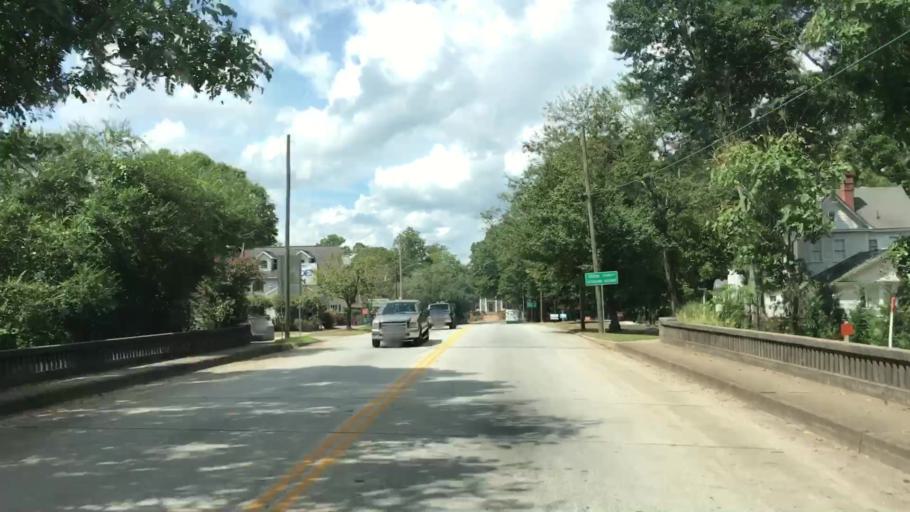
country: US
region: Georgia
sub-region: Greene County
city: Greensboro
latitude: 33.5762
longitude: -83.1860
